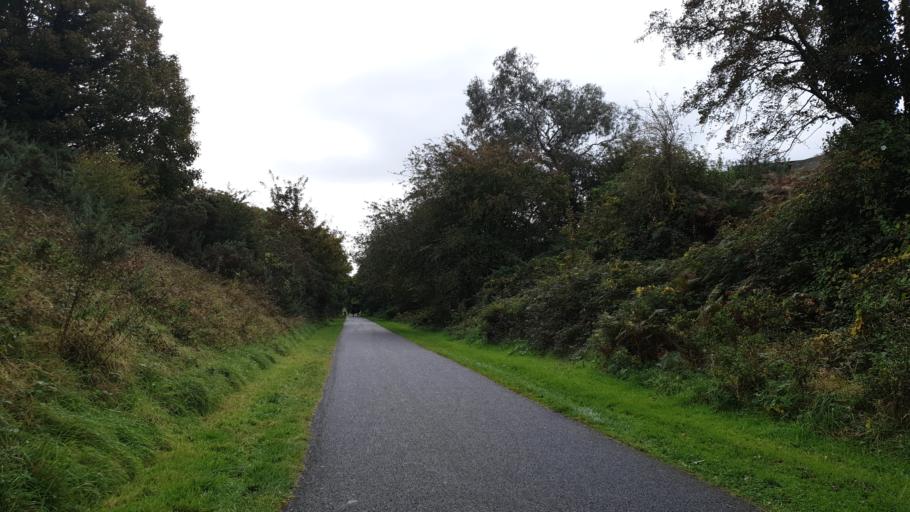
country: IE
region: Munster
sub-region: County Cork
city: Cork
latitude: 51.8922
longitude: -8.4138
